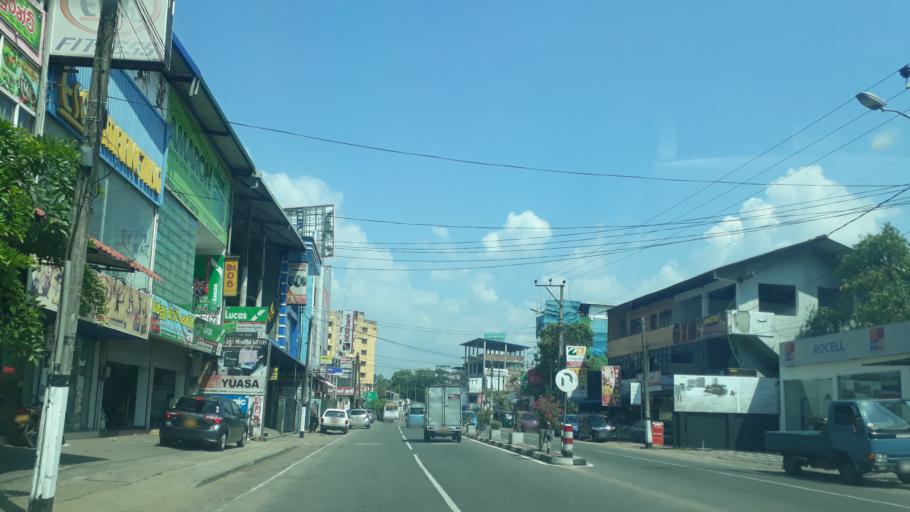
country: LK
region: Western
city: Gampaha
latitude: 7.0912
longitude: 79.9981
